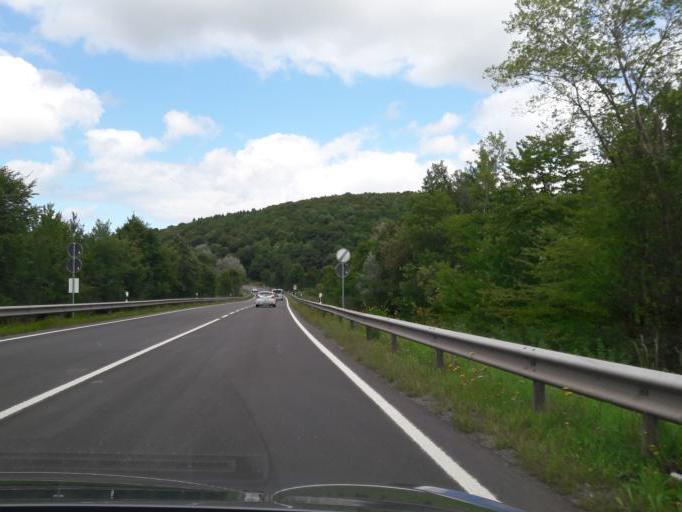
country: DE
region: Rheinland-Pfalz
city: Fohren-Linden
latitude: 49.5864
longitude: 7.2947
